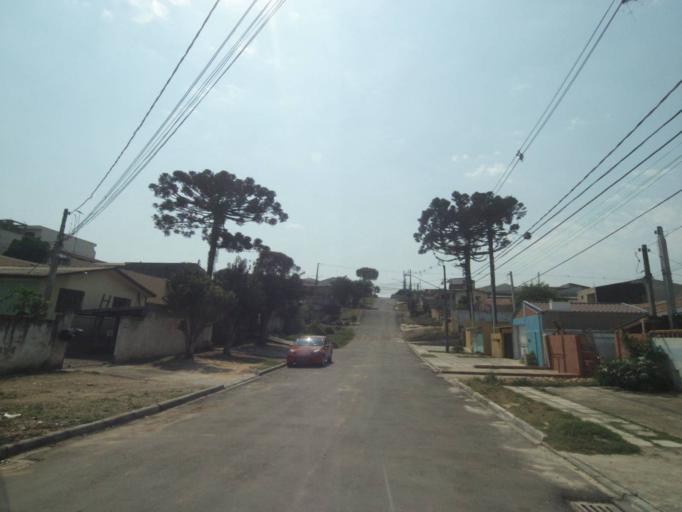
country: BR
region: Parana
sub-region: Sao Jose Dos Pinhais
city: Sao Jose dos Pinhais
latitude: -25.5383
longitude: -49.2484
